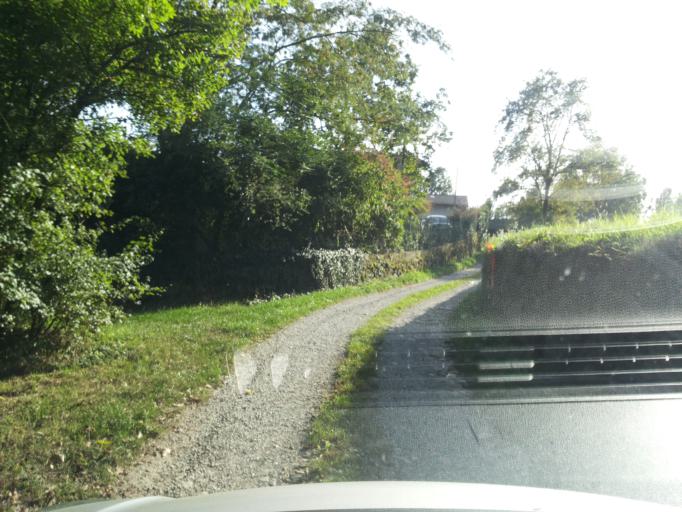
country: IT
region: Piedmont
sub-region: Provincia di Biella
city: Roppolo
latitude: 45.4354
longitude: 8.0755
